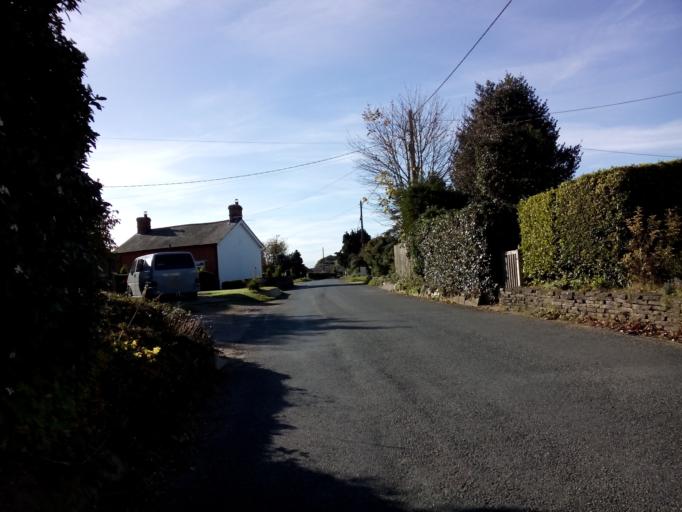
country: GB
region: England
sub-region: Suffolk
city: Bramford
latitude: 52.0280
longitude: 1.1075
